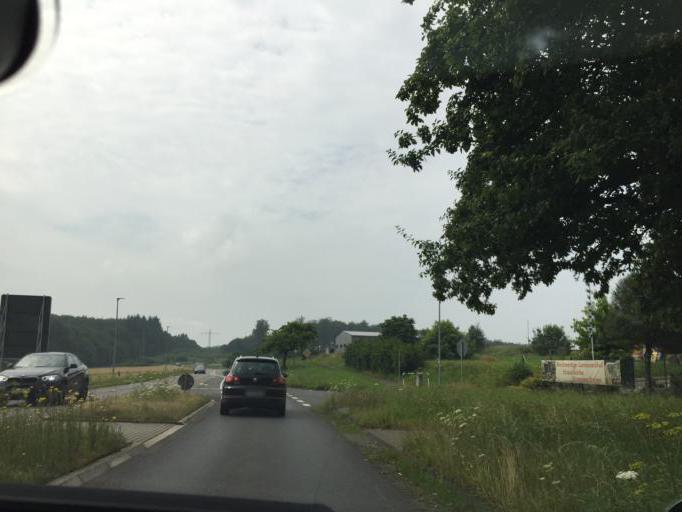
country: DE
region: Rheinland-Pfalz
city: Bonefeld
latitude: 50.5215
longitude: 7.4860
